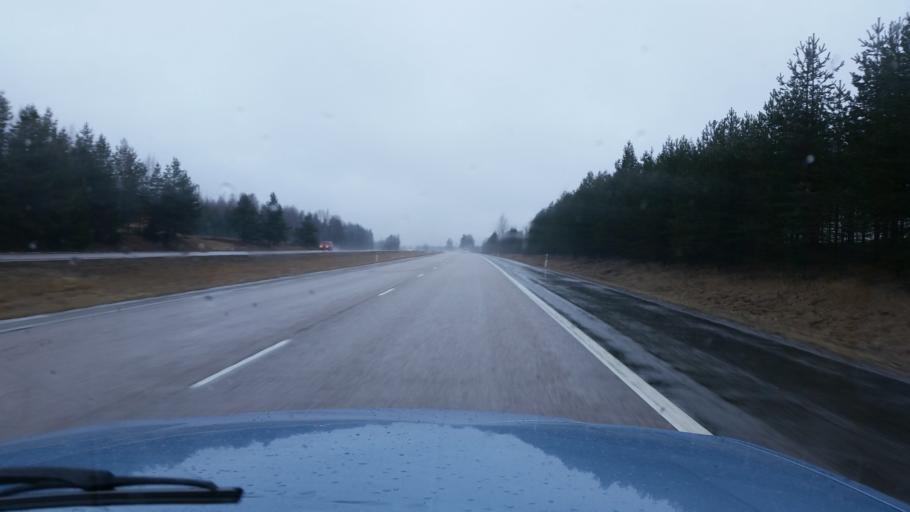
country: FI
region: Uusimaa
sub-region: Helsinki
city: Nurmijaervi
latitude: 60.4912
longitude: 24.8516
